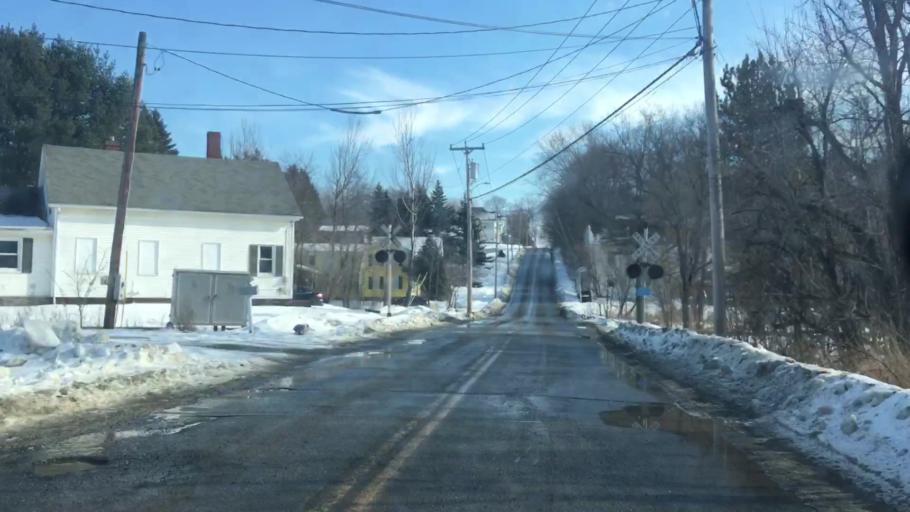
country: US
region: Maine
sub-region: Penobscot County
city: Bangor
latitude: 44.7702
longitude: -68.7794
